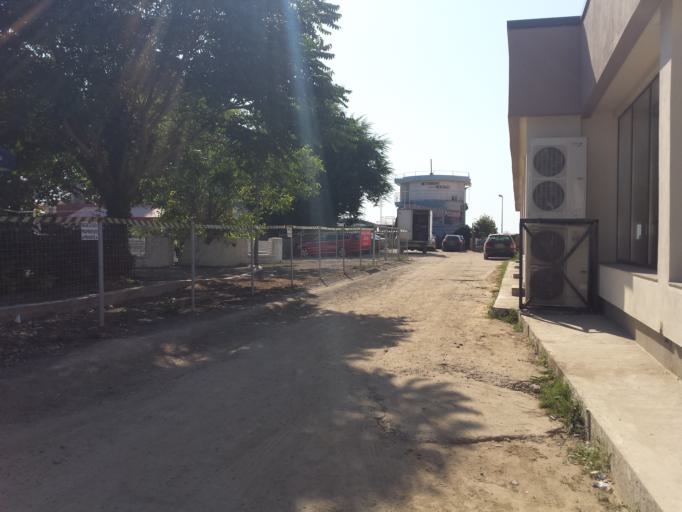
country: RO
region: Constanta
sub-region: Municipiul Mangalia
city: Mangalia
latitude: 43.8580
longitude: 28.6060
